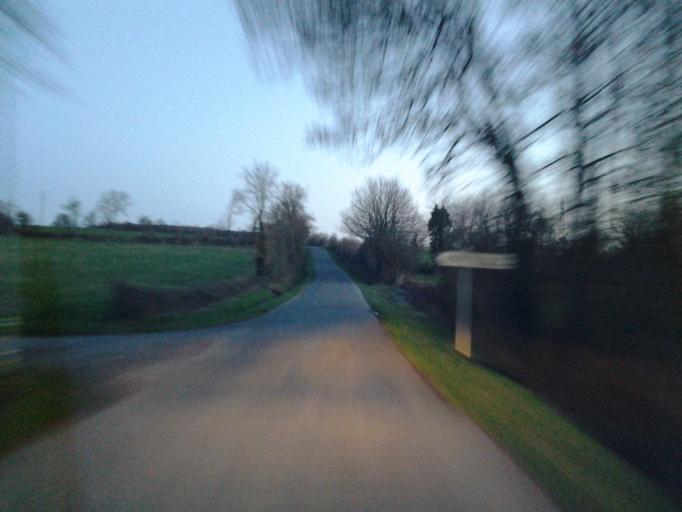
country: FR
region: Pays de la Loire
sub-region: Departement de la Vendee
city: Nesmy
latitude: 46.5930
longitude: -1.3629
